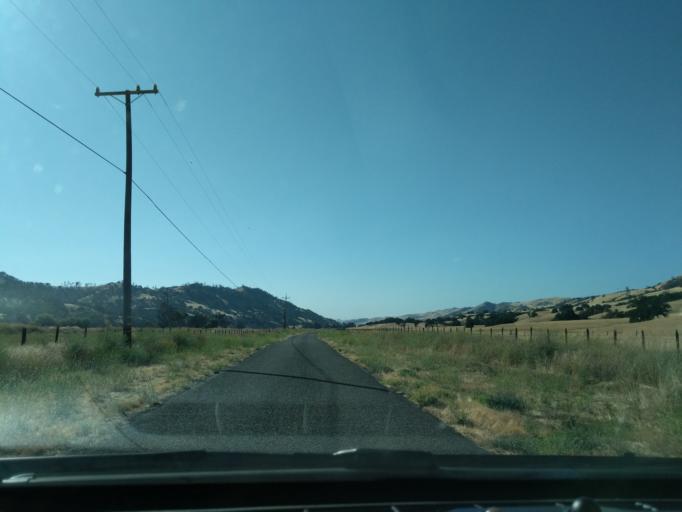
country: US
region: California
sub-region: San Luis Obispo County
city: San Miguel
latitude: 36.1192
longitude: -120.7314
